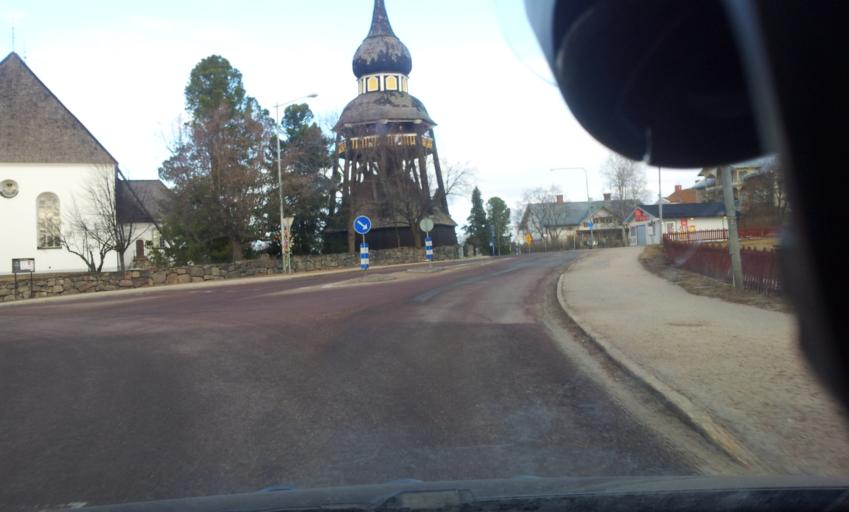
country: SE
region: Gaevleborg
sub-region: Ljusdals Kommun
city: Ljusdal
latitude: 61.8282
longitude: 16.0748
